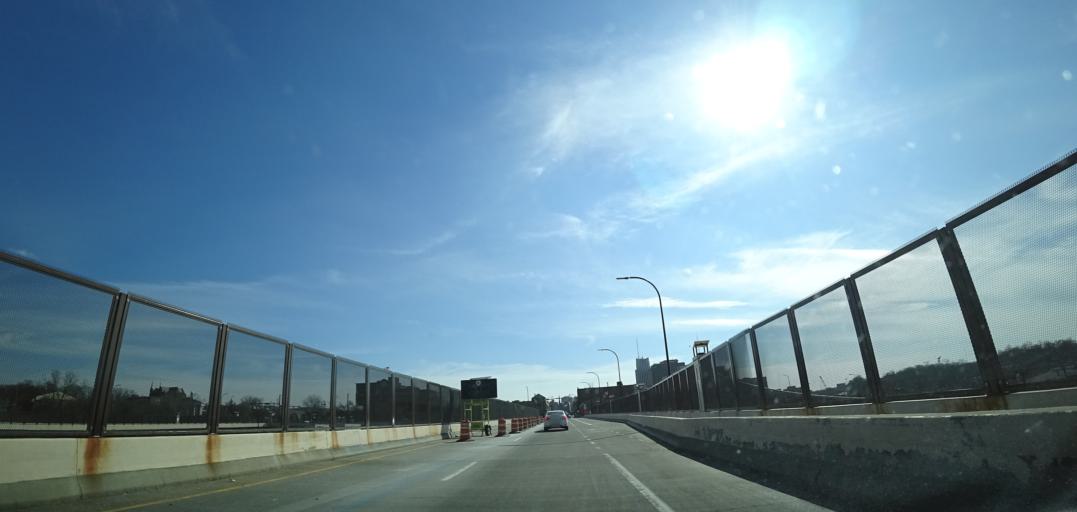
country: US
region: Ohio
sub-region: Summit County
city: Akron
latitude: 41.0887
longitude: -81.5139
